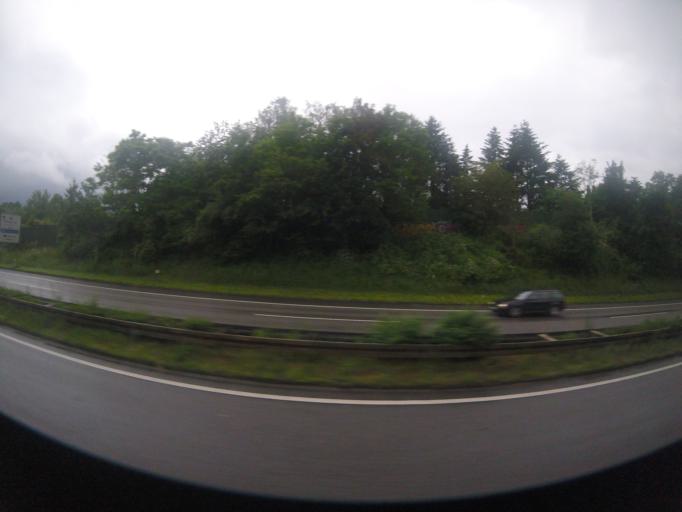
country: DE
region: Saarland
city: Bexbach
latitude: 49.3245
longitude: 7.2329
